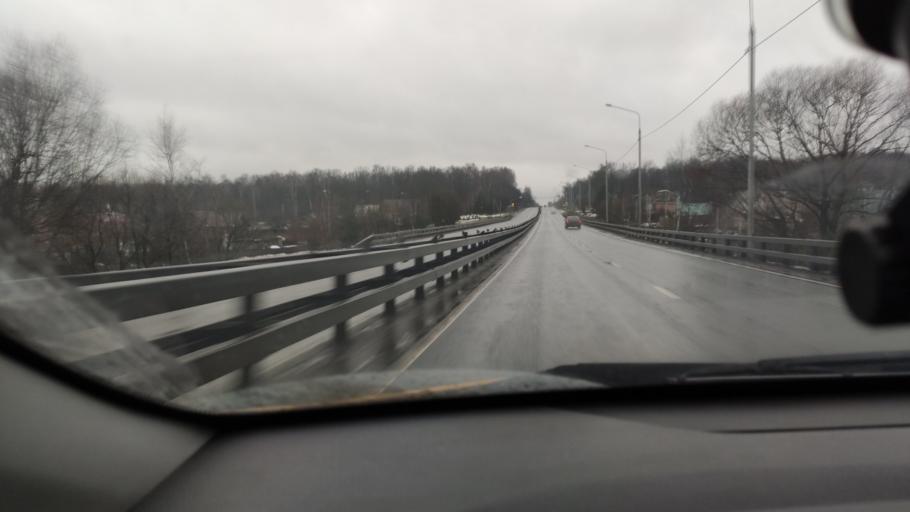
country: RU
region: Moskovskaya
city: Troitsk
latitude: 55.3222
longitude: 37.2609
